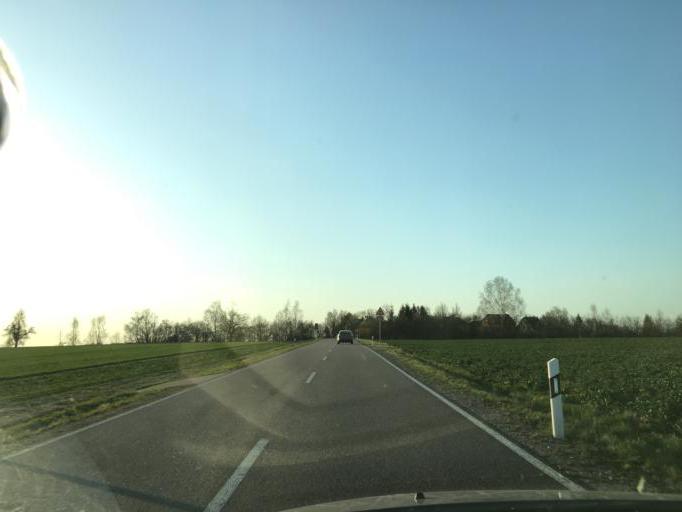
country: DE
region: Saxony
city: Narsdorf
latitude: 51.0152
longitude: 12.7342
